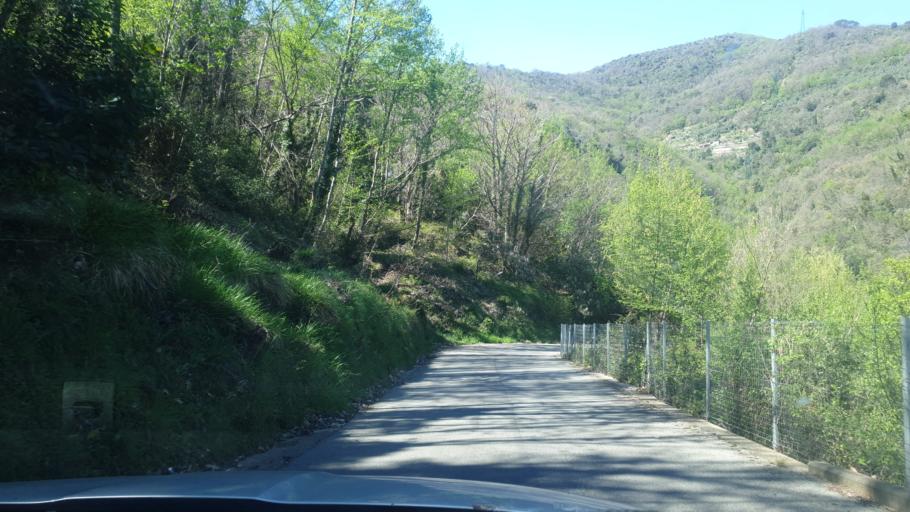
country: IT
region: Liguria
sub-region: Provincia di Genova
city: Recco
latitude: 44.3762
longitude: 9.1441
